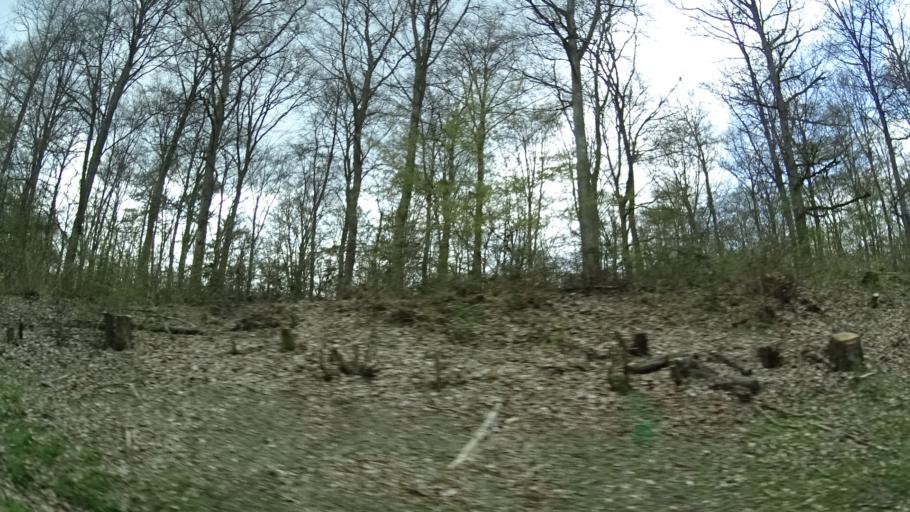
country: DE
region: Rheinland-Pfalz
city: Langenthal
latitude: 49.8605
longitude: 7.5794
